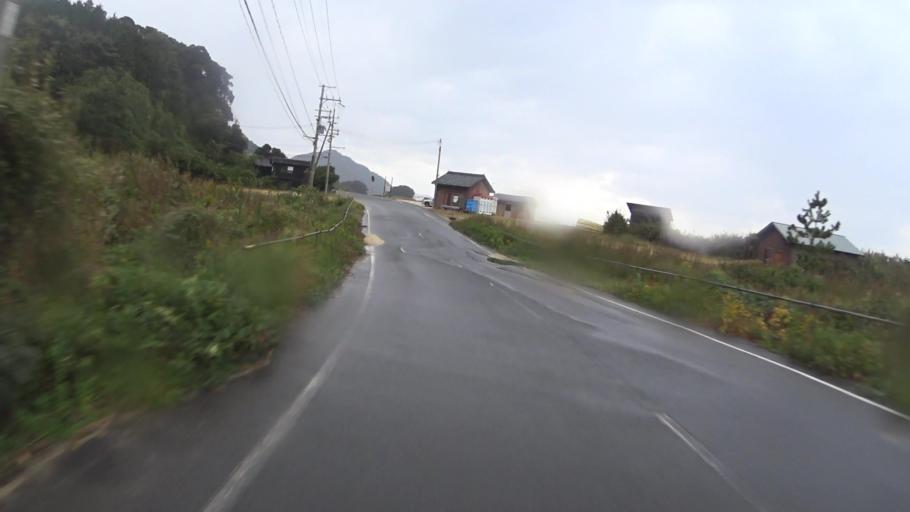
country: JP
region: Kyoto
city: Miyazu
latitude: 35.5676
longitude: 135.2524
